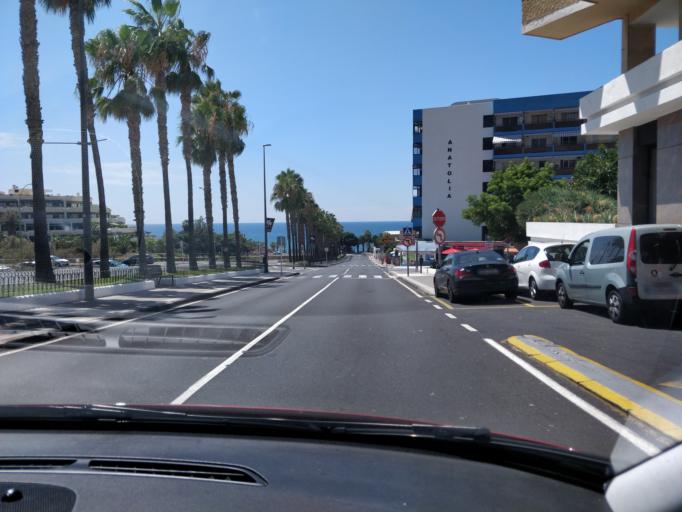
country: ES
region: Canary Islands
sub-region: Provincia de Santa Cruz de Tenerife
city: Puerto de la Cruz
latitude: 28.4114
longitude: -16.5563
